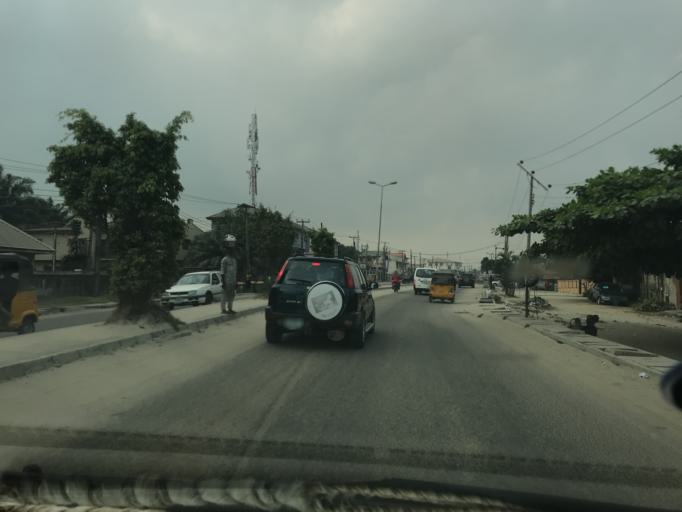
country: NG
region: Lagos
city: Ikoyi
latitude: 6.4750
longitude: 3.5678
